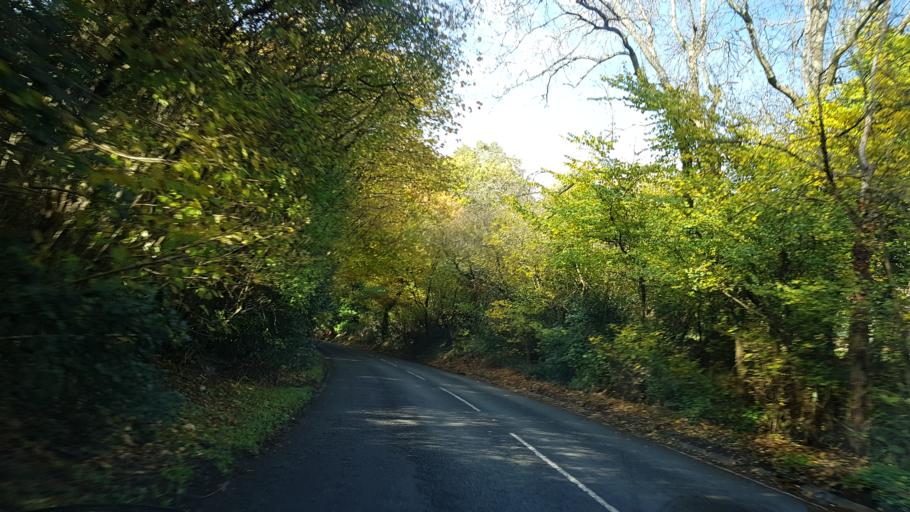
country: GB
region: England
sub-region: Surrey
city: Elstead
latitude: 51.1895
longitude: -0.7179
